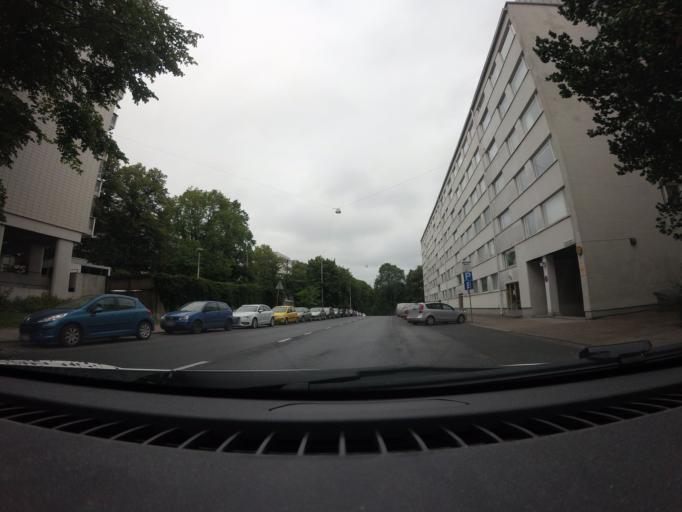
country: FI
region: Varsinais-Suomi
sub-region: Turku
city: Turku
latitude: 60.4548
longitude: 22.2742
